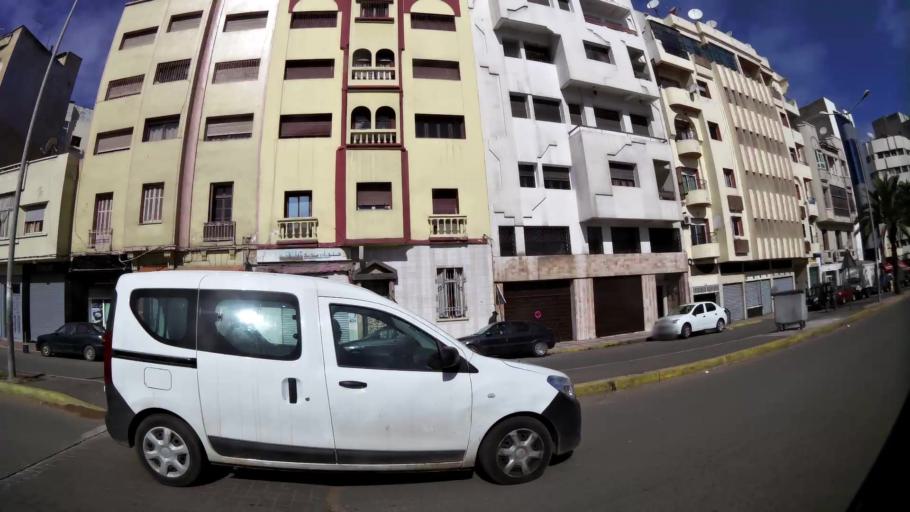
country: MA
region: Grand Casablanca
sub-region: Casablanca
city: Casablanca
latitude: 33.5939
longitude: -7.5935
